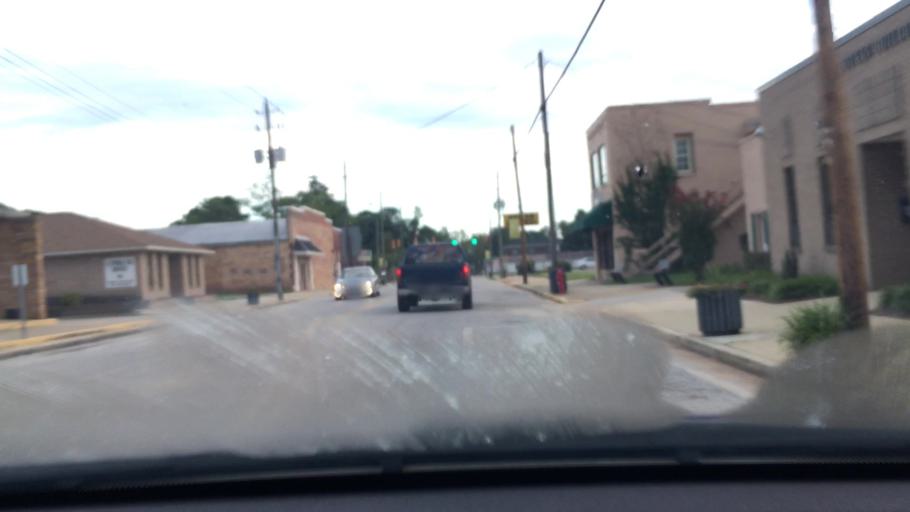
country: US
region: South Carolina
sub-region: Florence County
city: Timmonsville
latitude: 34.1696
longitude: -80.0636
